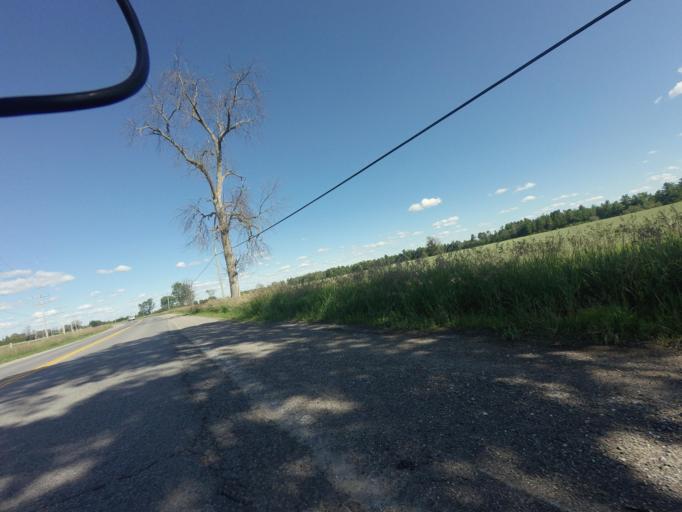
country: CA
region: Ontario
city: Arnprior
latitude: 45.4163
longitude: -76.4159
